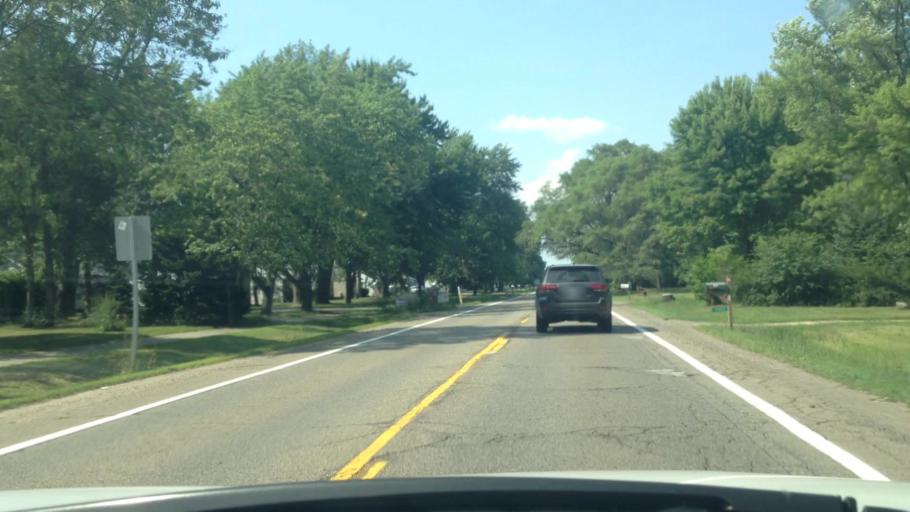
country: US
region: Michigan
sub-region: Oakland County
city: Waterford
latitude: 42.7131
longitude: -83.3786
